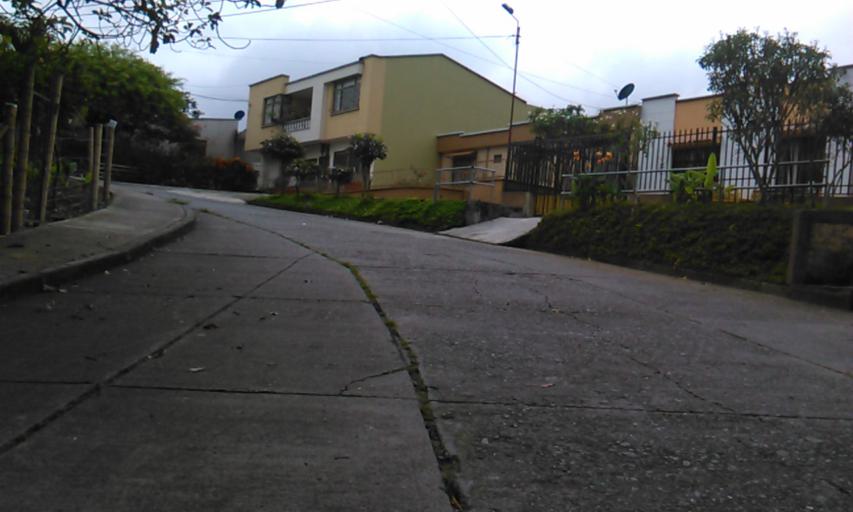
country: CO
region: Quindio
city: Armenia
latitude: 4.5225
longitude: -75.6886
